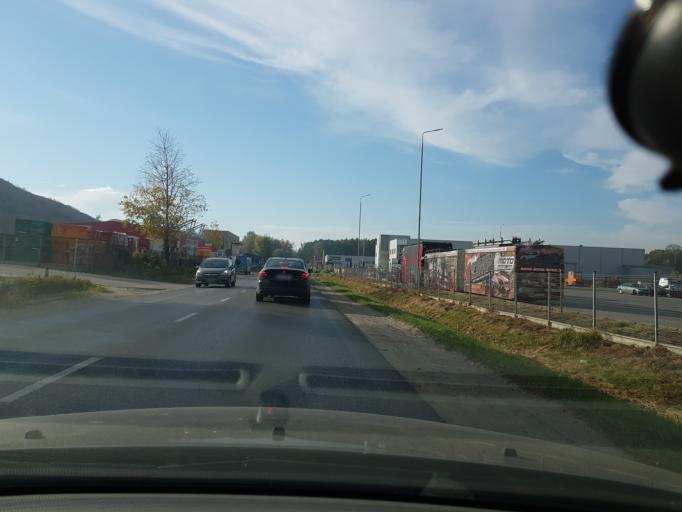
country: PL
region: Masovian Voivodeship
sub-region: Powiat warszawski zachodni
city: Babice
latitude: 52.2783
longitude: 20.8756
